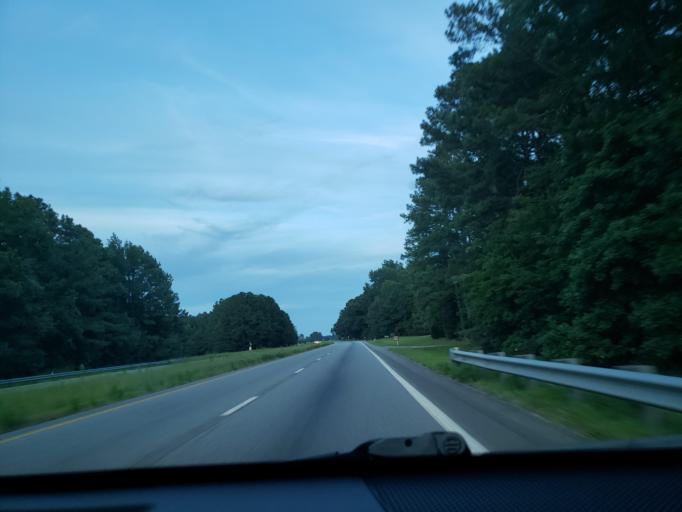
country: US
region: Virginia
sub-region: Southampton County
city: Courtland
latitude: 36.7074
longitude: -77.1541
